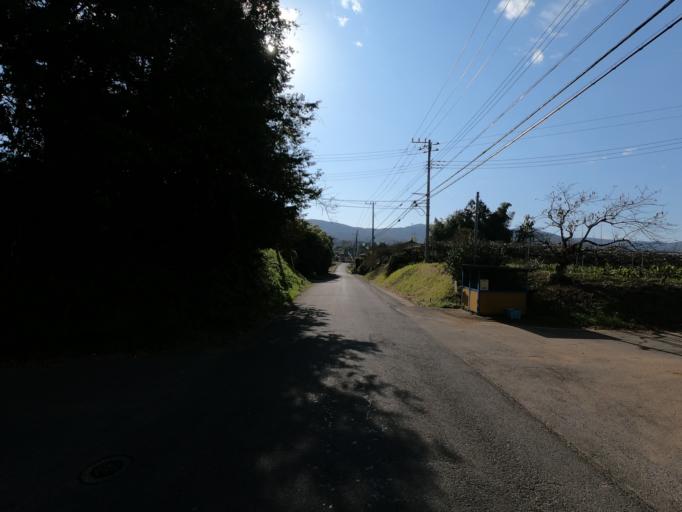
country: JP
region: Ibaraki
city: Tsukuba
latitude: 36.1898
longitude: 140.1802
